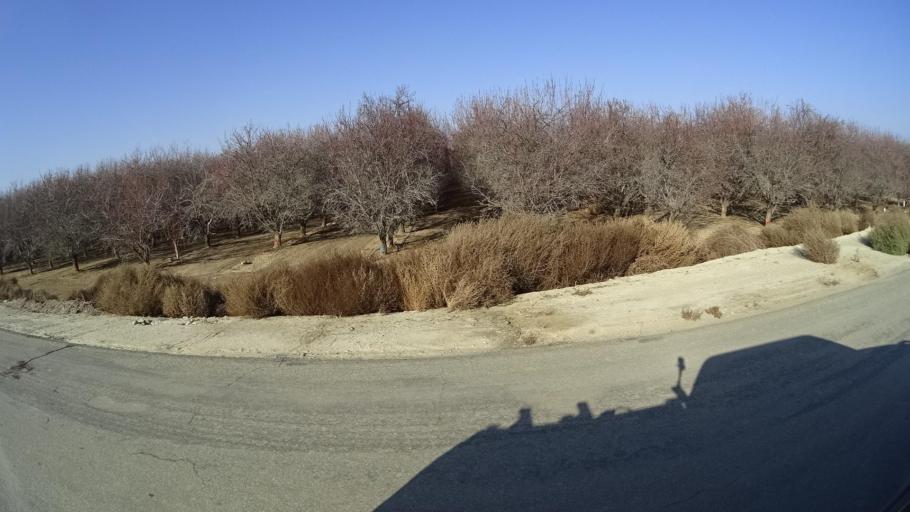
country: US
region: California
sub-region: Kern County
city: Maricopa
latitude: 35.1013
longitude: -119.3505
